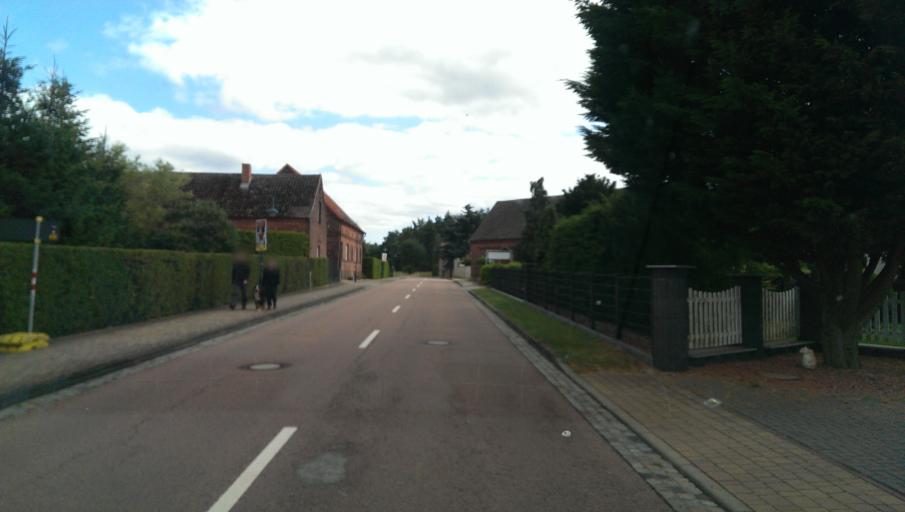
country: DE
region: Saxony-Anhalt
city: Radis
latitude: 51.7822
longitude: 12.4862
